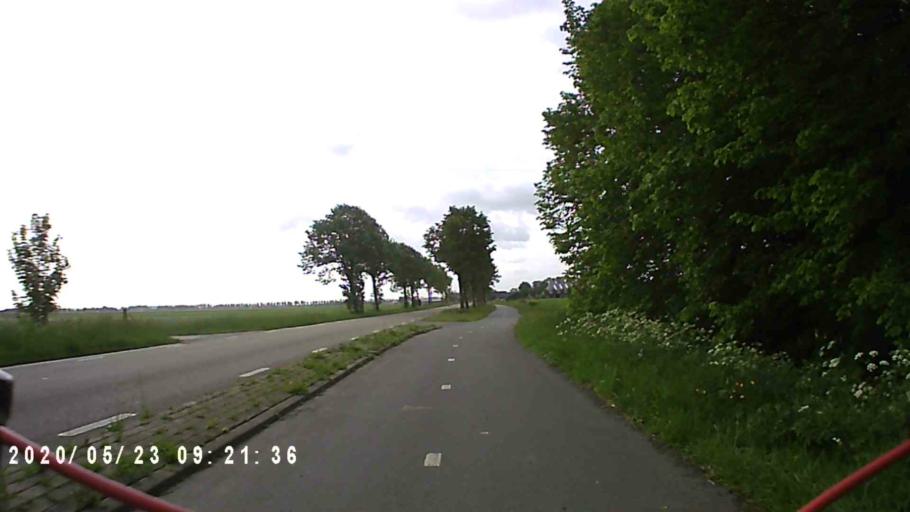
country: NL
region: Groningen
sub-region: Gemeente Bedum
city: Bedum
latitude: 53.2926
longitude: 6.6774
